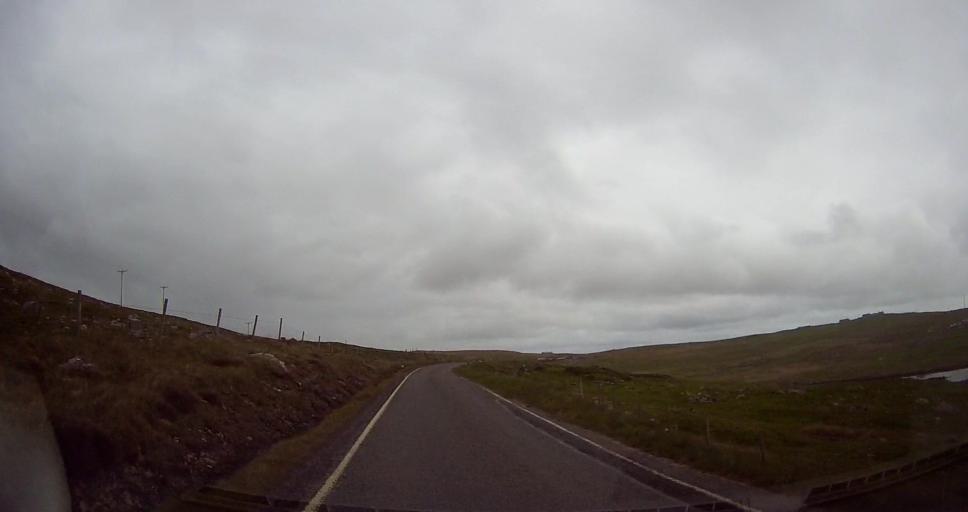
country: GB
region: Scotland
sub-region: Shetland Islands
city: Sandwick
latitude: 60.2440
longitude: -1.5177
